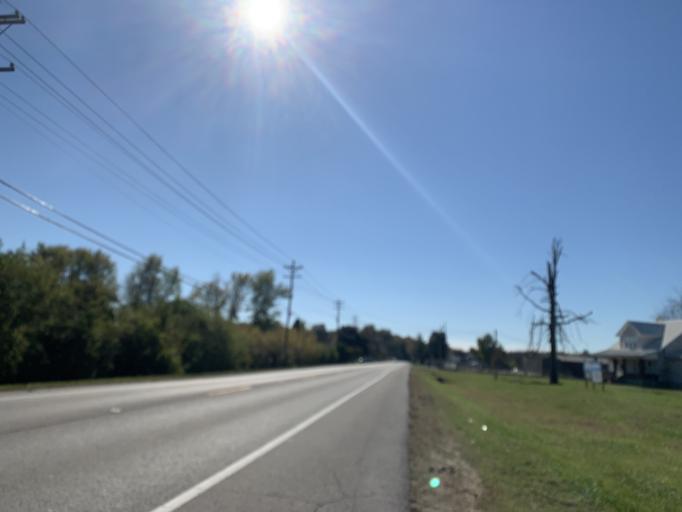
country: US
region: Kentucky
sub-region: Jefferson County
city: Saint Dennis
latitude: 38.2020
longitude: -85.8550
